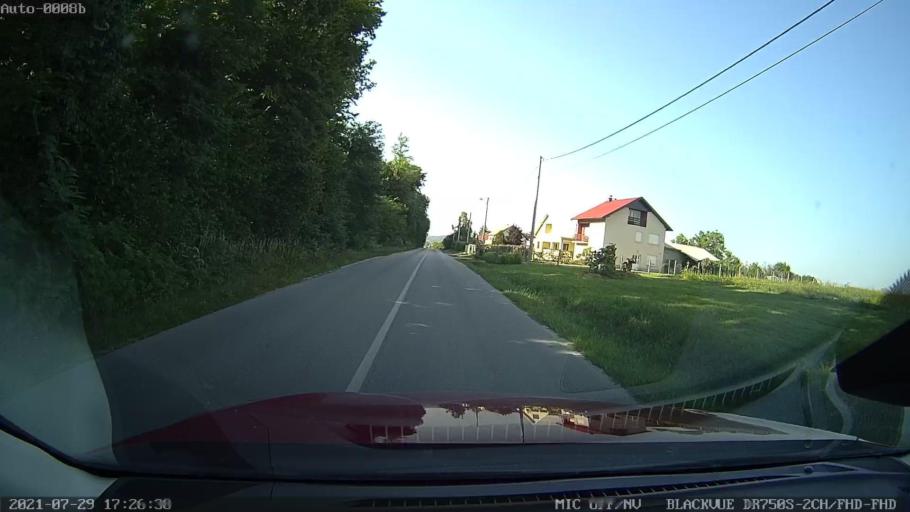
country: HR
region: Varazdinska
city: Ivanec
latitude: 46.2551
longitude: 16.1175
